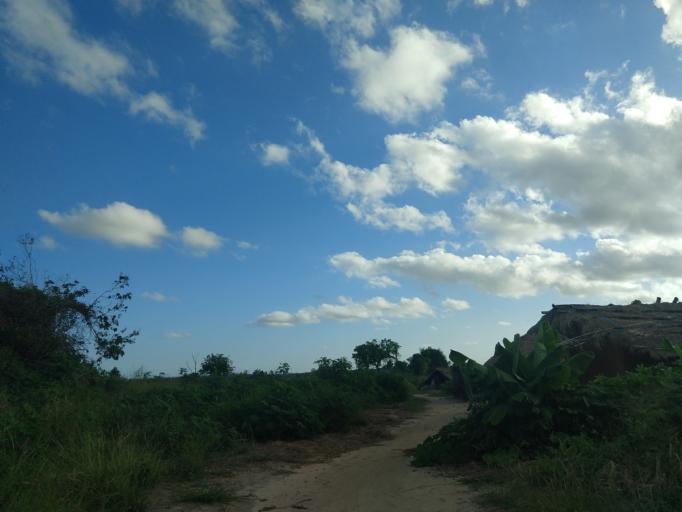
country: MZ
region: Sofala
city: Beira
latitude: -19.6085
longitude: 35.1449
